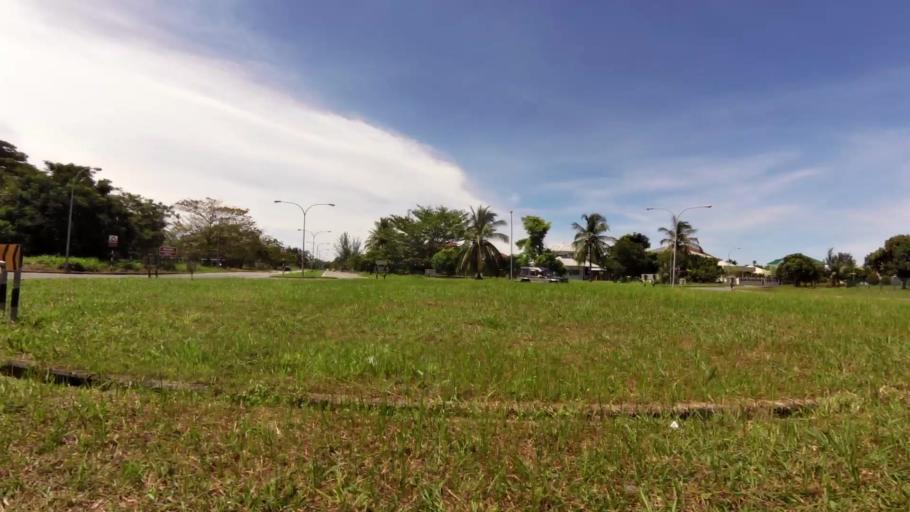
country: BN
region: Belait
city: Kuala Belait
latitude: 4.5865
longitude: 114.2315
